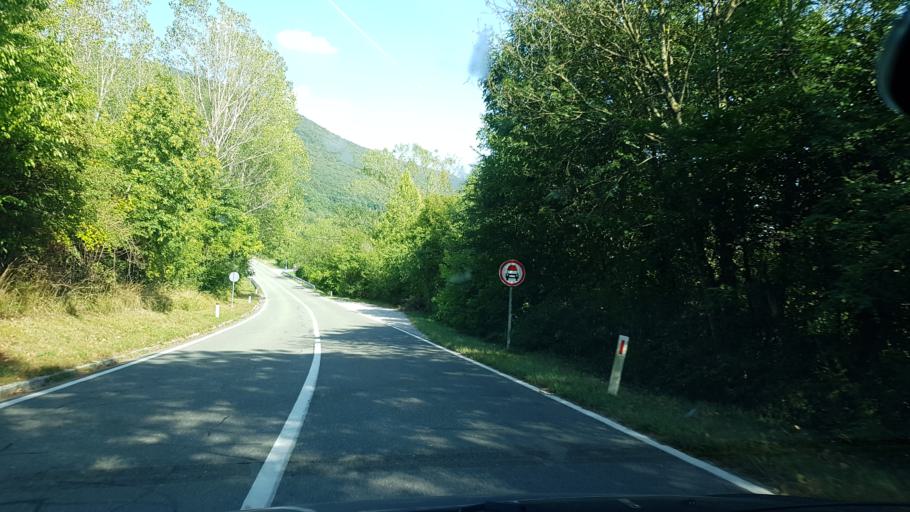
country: IT
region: Friuli Venezia Giulia
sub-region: Provincia di Gorizia
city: San Floriano del Collio
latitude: 45.9867
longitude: 13.6090
